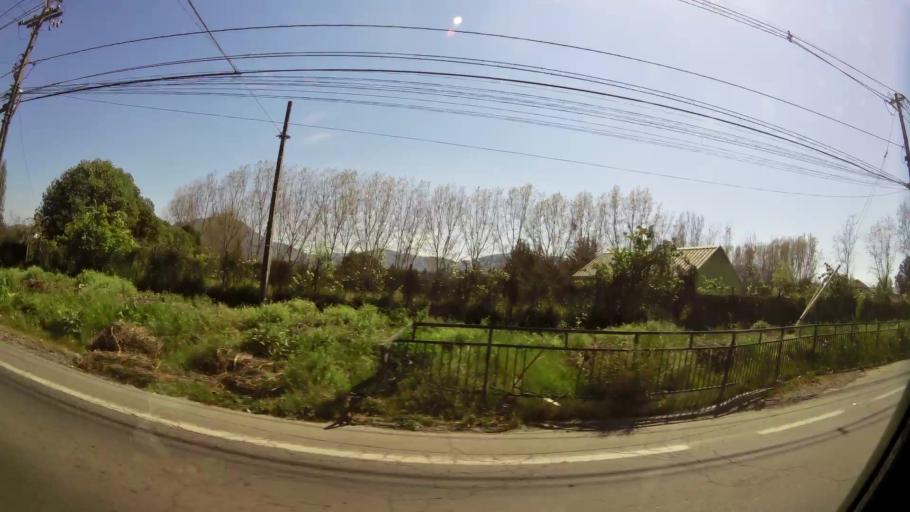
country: CL
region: Santiago Metropolitan
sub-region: Provincia de Talagante
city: Talagante
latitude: -33.6396
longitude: -70.9133
